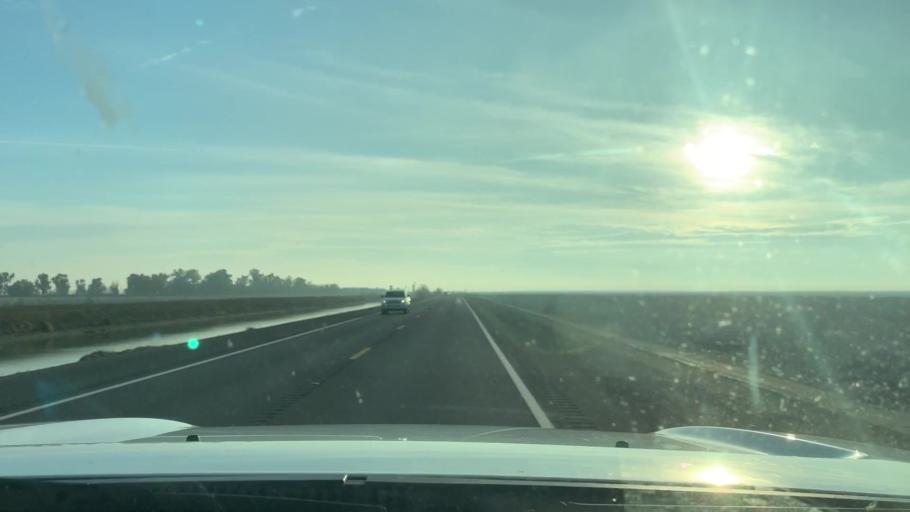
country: US
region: California
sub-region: Kings County
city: Stratford
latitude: 36.1314
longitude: -119.8846
